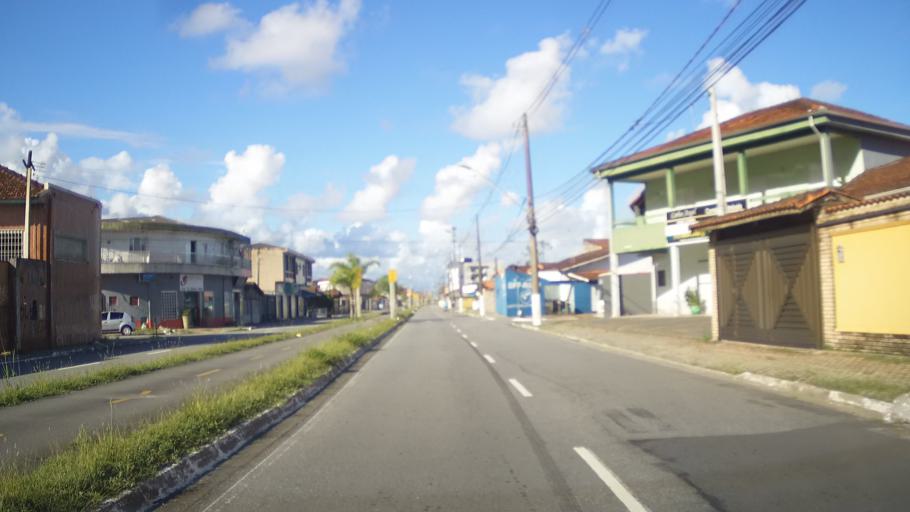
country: BR
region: Sao Paulo
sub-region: Mongagua
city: Mongagua
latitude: -24.0575
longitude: -46.5522
